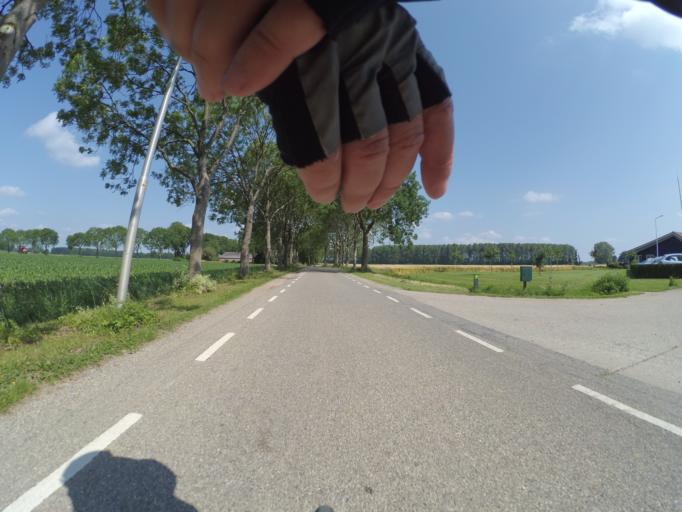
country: NL
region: Gelderland
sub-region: Gemeente Culemborg
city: Culemborg
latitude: 51.9401
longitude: 5.1821
